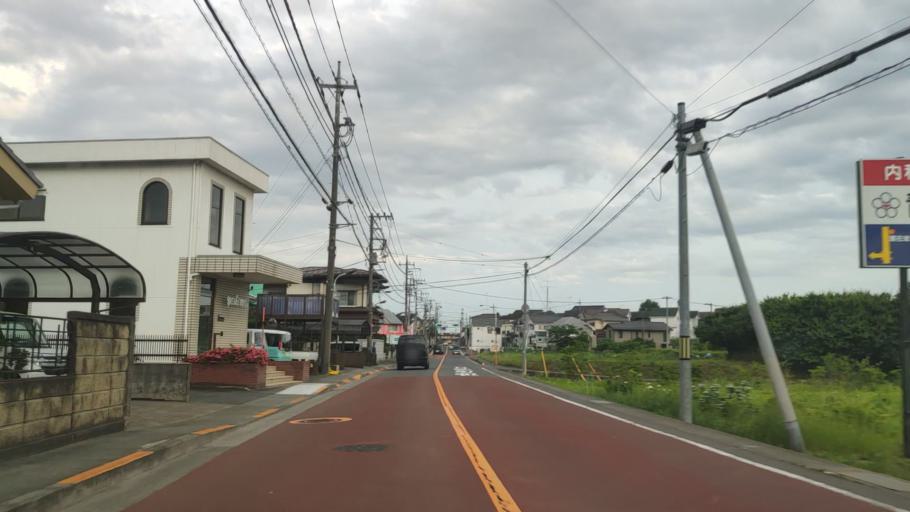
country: JP
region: Saitama
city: Hanno
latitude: 35.8073
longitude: 139.3044
